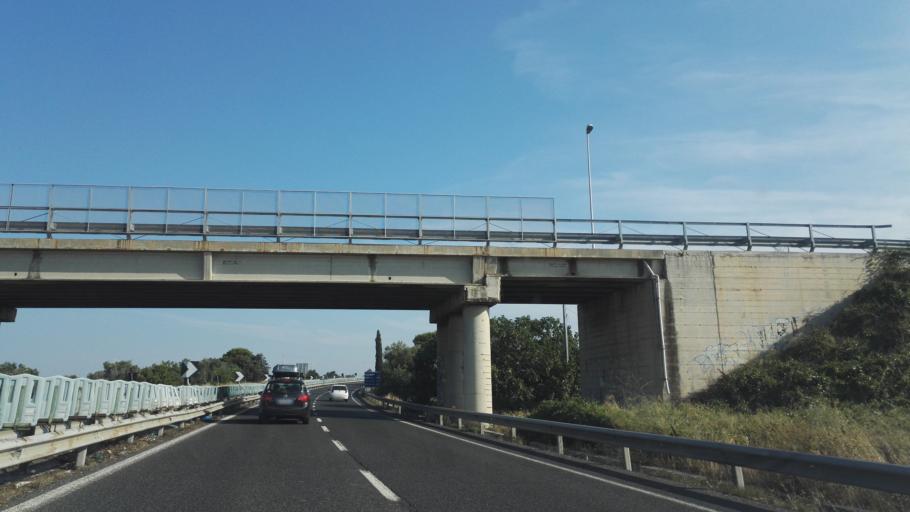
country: IT
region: Apulia
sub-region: Provincia di Bari
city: Mola di Bari
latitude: 41.0693
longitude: 17.0654
